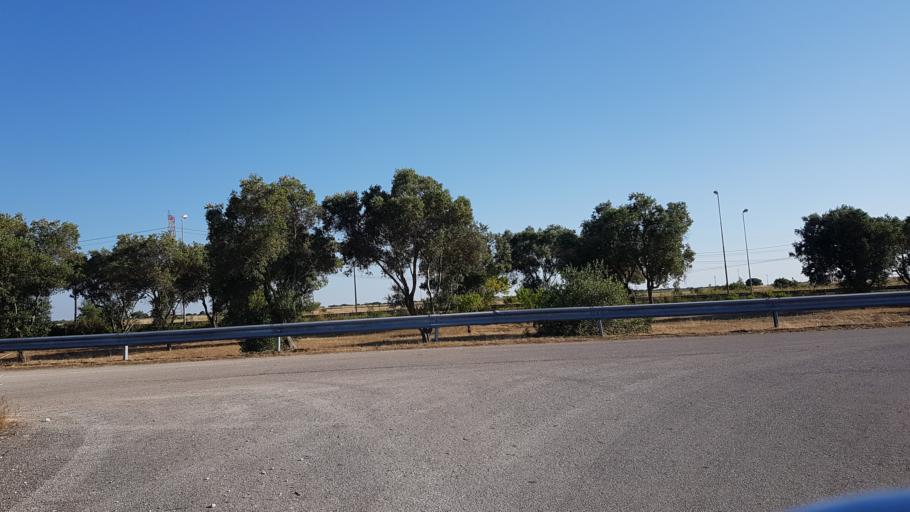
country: IT
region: Apulia
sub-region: Provincia di Brindisi
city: San Pietro Vernotico
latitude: 40.5597
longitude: 18.0204
